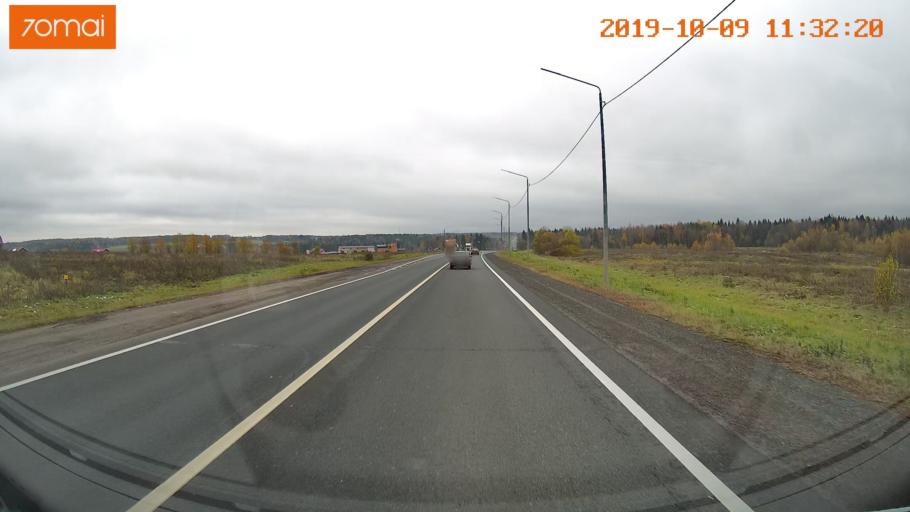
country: RU
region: Vologda
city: Gryazovets
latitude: 59.0369
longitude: 40.1071
